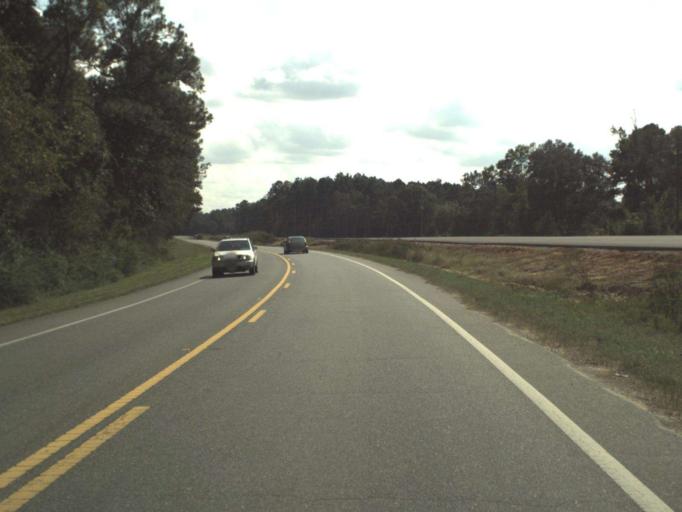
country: US
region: Florida
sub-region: Holmes County
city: Bonifay
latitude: 30.6575
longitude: -85.6994
